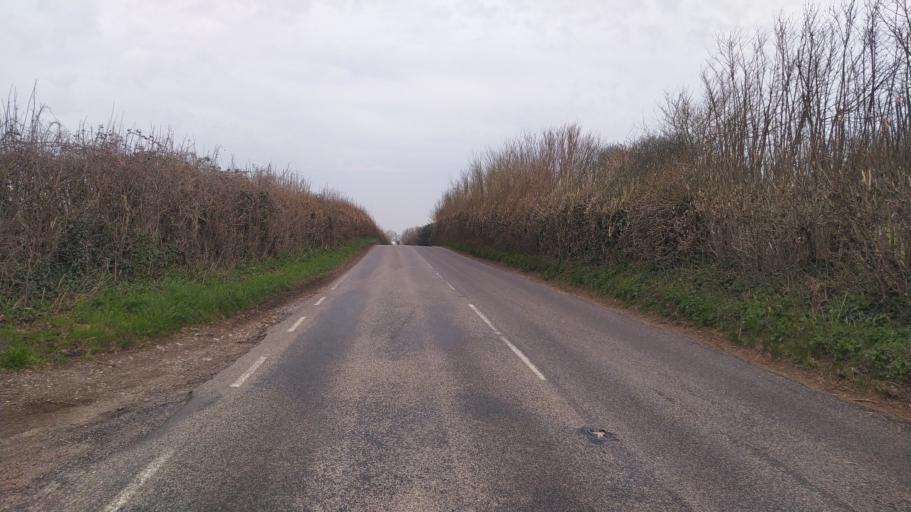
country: GB
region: England
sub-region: Dorset
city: Dorchester
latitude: 50.7641
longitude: -2.5568
